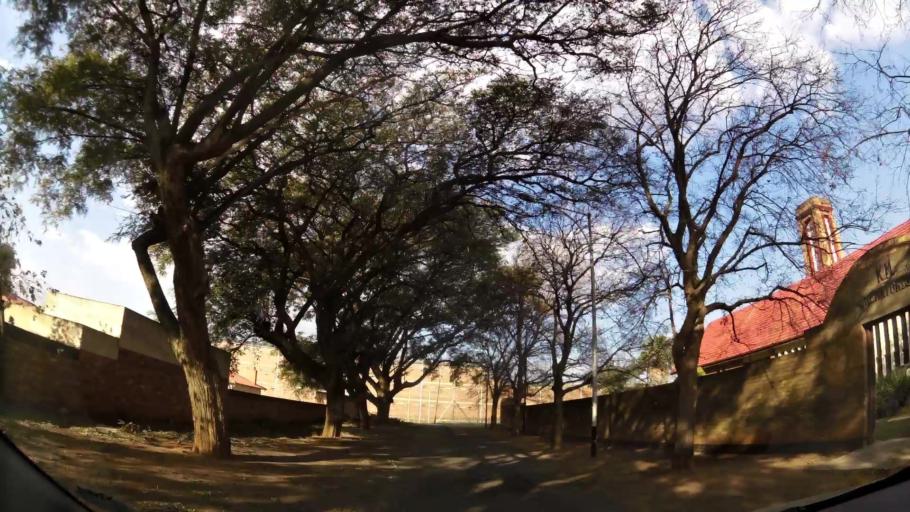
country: ZA
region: Gauteng
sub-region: West Rand District Municipality
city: Krugersdorp
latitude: -26.1015
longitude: 27.7618
